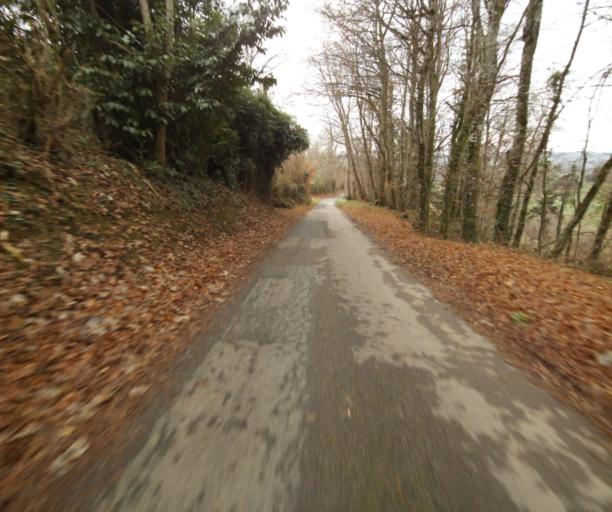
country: FR
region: Limousin
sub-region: Departement de la Correze
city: Laguenne
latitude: 45.2345
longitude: 1.7466
